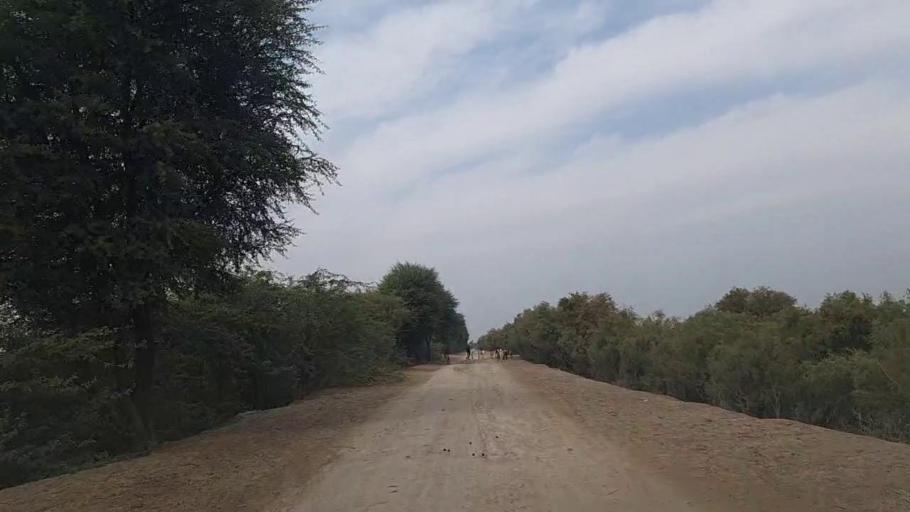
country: PK
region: Sindh
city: Daur
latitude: 26.4384
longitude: 68.4614
